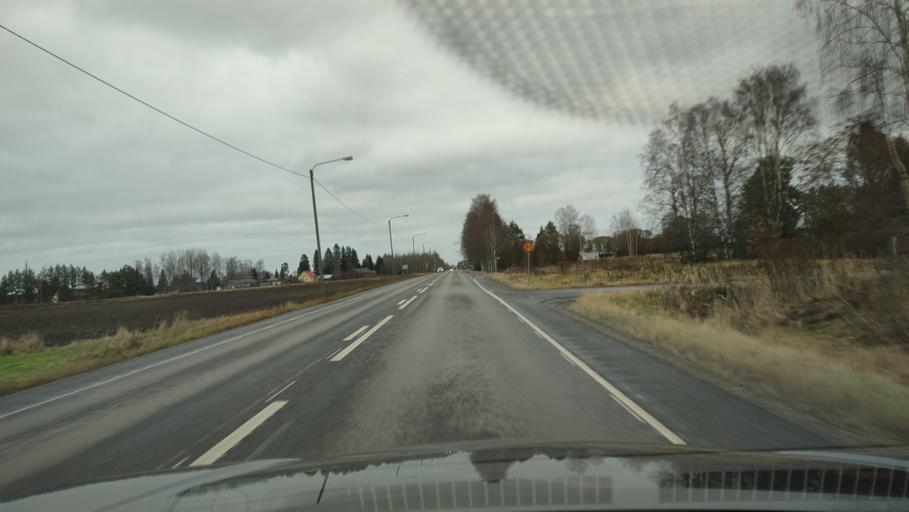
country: FI
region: Southern Ostrobothnia
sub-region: Seinaejoki
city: Ilmajoki
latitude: 62.6926
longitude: 22.4975
